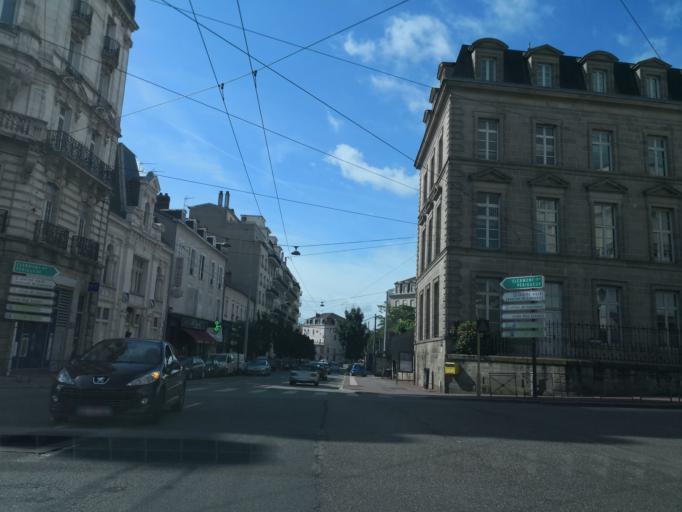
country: FR
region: Limousin
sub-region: Departement de la Haute-Vienne
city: Limoges
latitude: 45.8318
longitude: 1.2624
